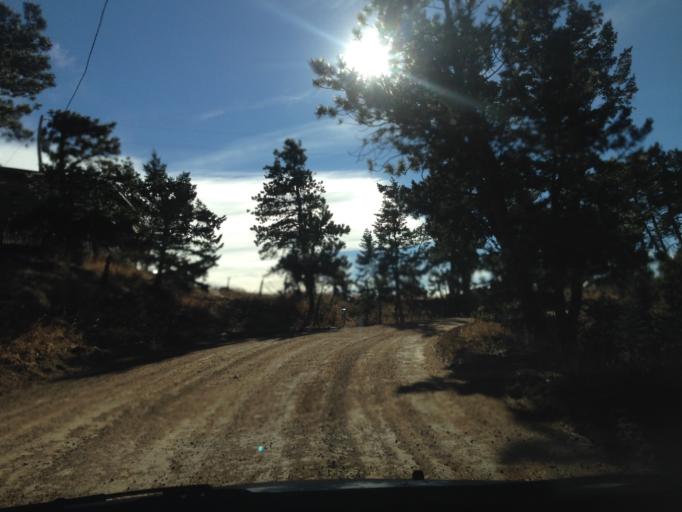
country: US
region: Colorado
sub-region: Boulder County
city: Coal Creek
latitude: 39.9144
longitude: -105.3494
